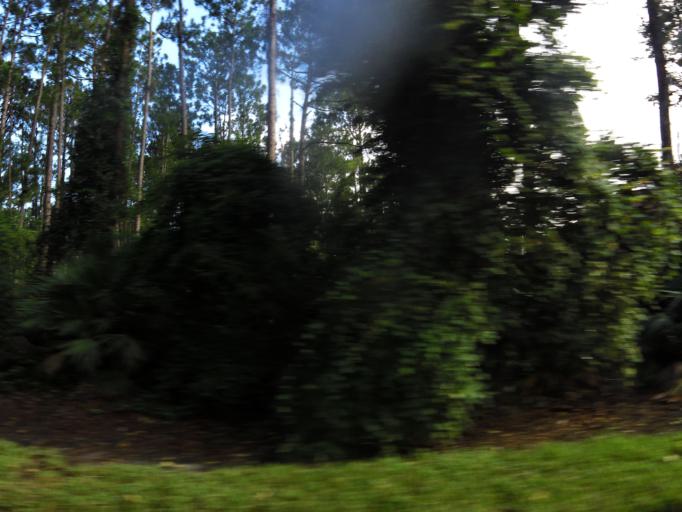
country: US
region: Florida
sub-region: Saint Johns County
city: Fruit Cove
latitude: 30.2116
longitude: -81.5362
